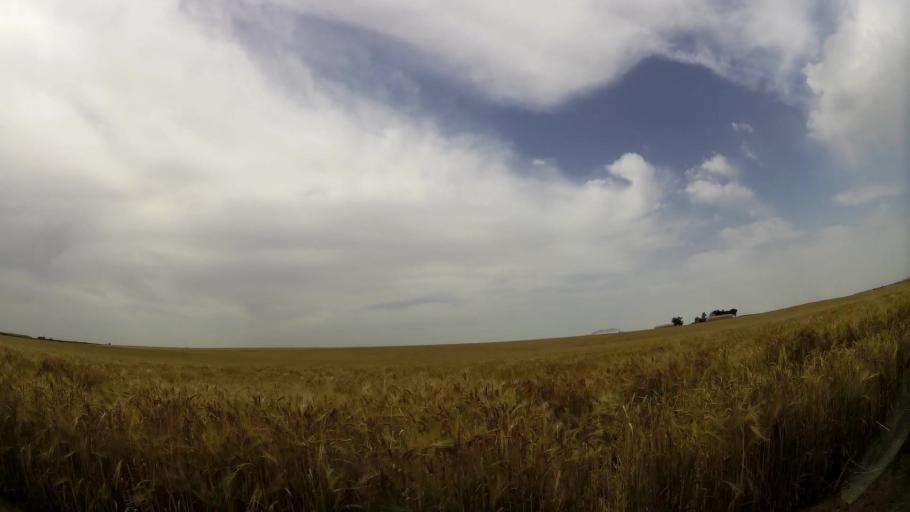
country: MA
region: Rabat-Sale-Zemmour-Zaer
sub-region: Khemisset
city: Tiflet
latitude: 33.7581
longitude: -6.2182
